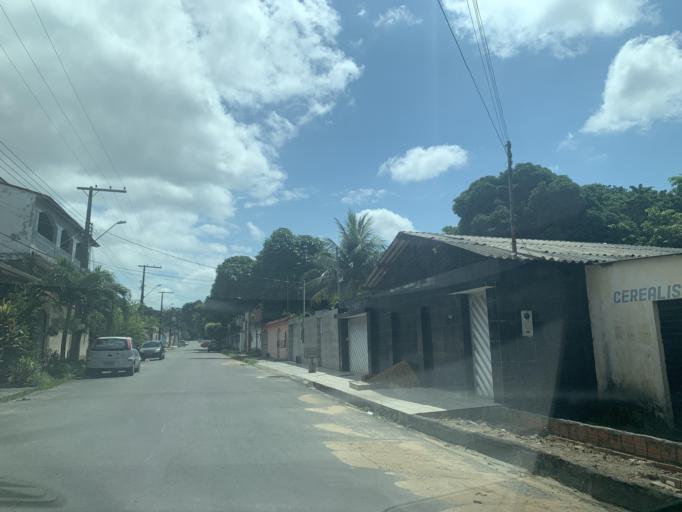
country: BR
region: Amazonas
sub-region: Manaus
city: Manaus
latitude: -3.1039
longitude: -59.9630
